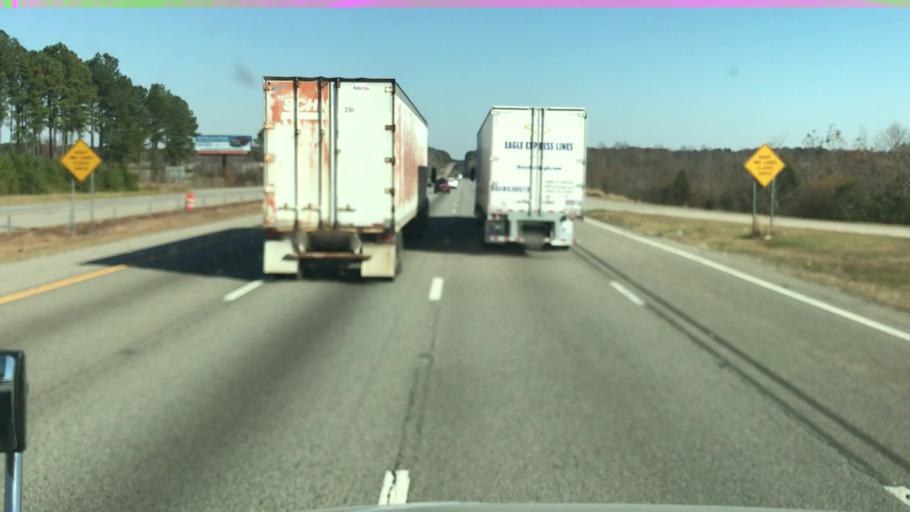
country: US
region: North Carolina
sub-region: Wake County
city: Wendell
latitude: 35.8076
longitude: -78.4204
